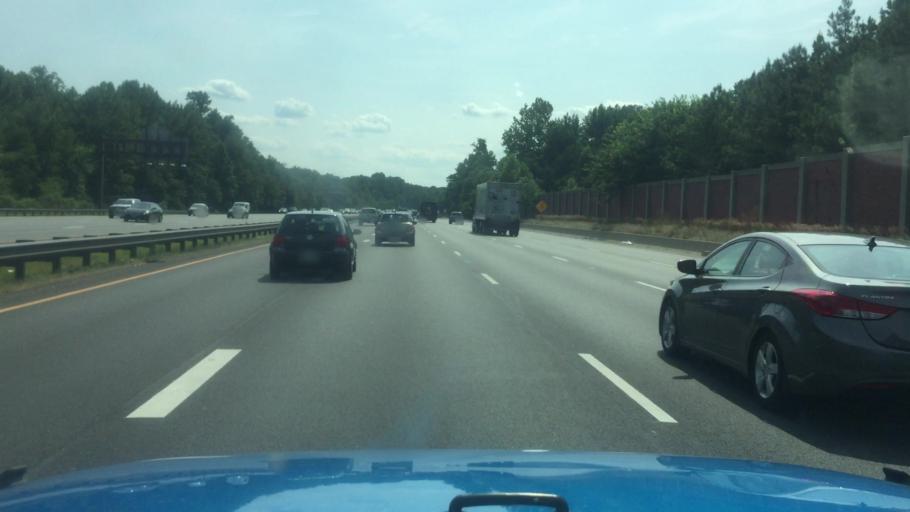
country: US
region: Maryland
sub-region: Prince George's County
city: Bowie
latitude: 38.9500
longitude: -76.7523
